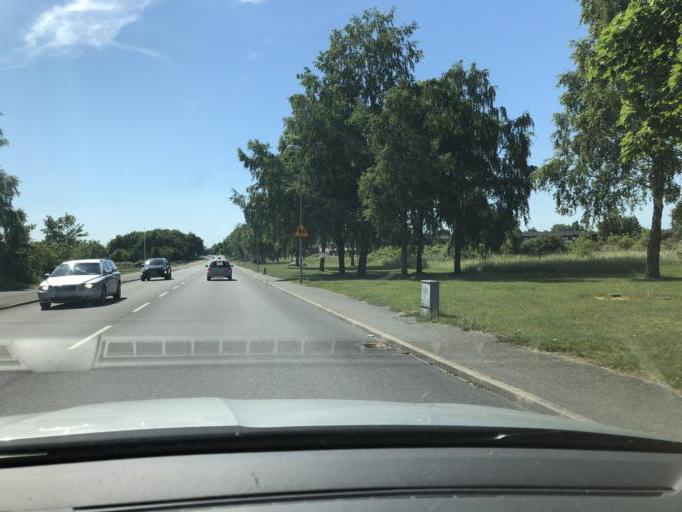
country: SE
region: Skane
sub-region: Bromolla Kommun
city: Bromoella
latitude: 56.0761
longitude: 14.4930
